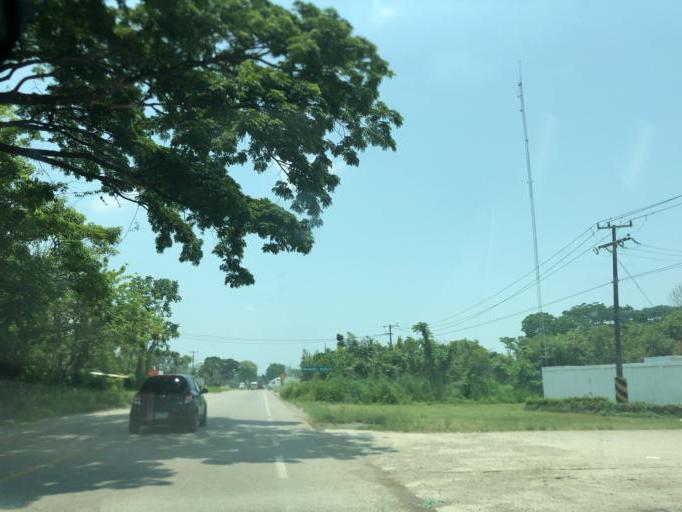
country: MX
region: Tabasco
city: Teapa
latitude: 17.5891
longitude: -92.9662
